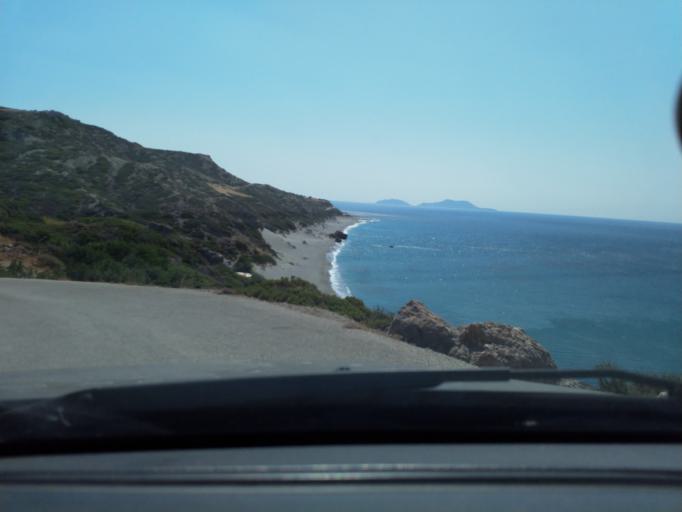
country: GR
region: Crete
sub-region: Nomos Rethymnis
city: Agia Foteini
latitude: 35.1393
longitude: 24.5286
